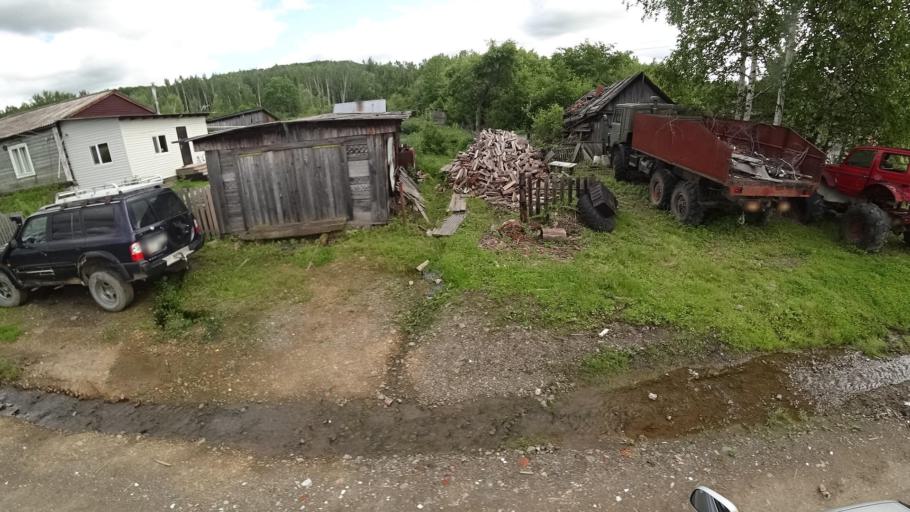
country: RU
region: Khabarovsk Krai
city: Litovko
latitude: 49.3636
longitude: 135.1688
